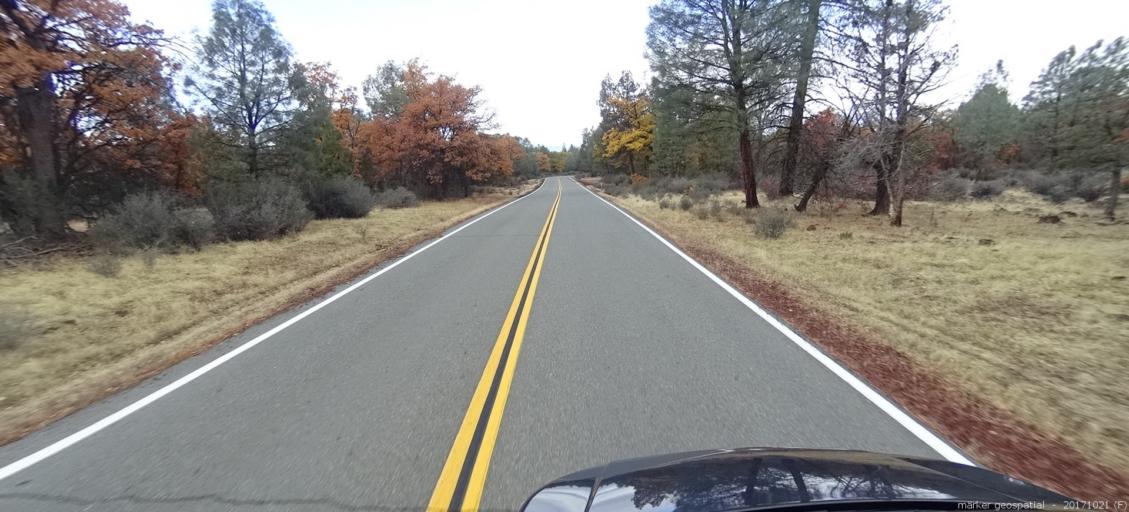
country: US
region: California
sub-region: Shasta County
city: Burney
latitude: 40.9240
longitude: -121.5241
